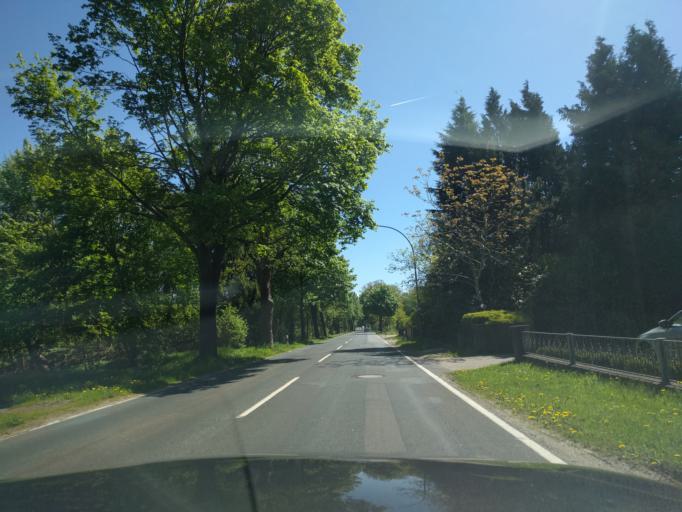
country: DE
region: Lower Saxony
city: Seevetal
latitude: 53.4008
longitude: 10.0060
